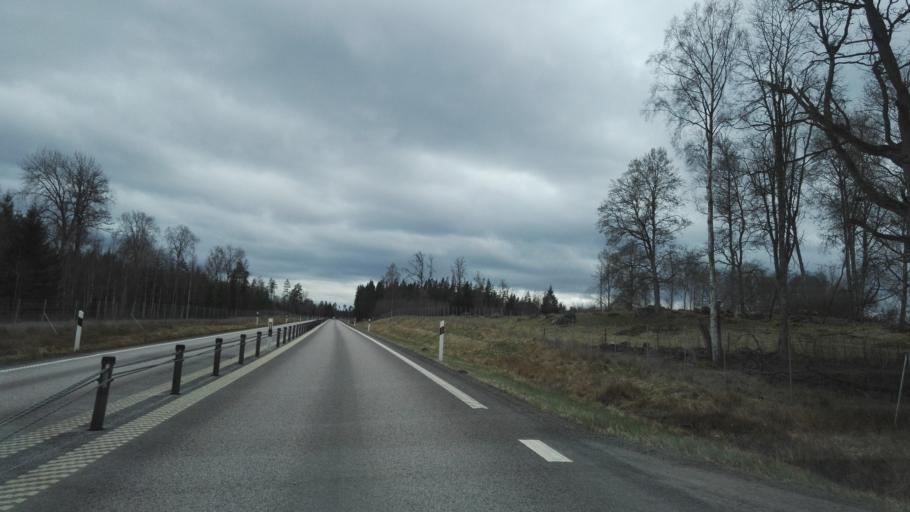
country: SE
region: Kronoberg
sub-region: Alvesta Kommun
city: Vislanda
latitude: 56.6812
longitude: 14.3167
